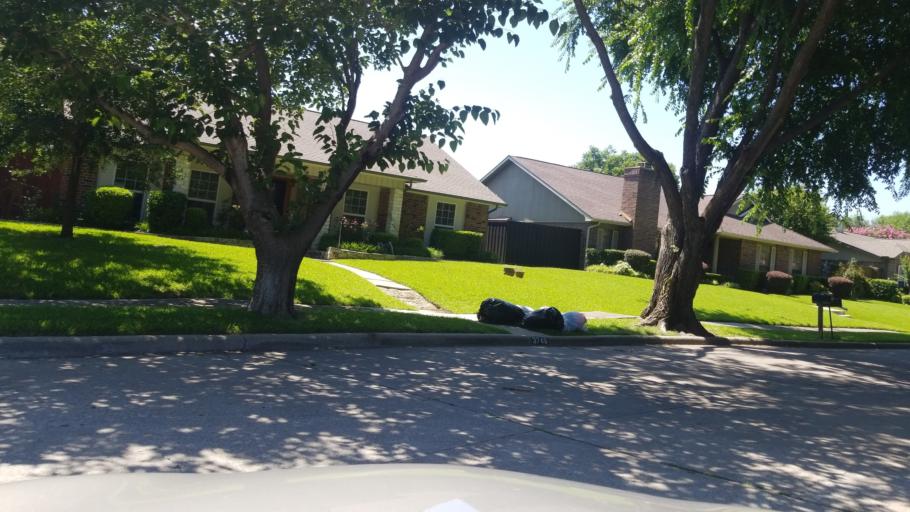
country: US
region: Texas
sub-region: Dallas County
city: Grand Prairie
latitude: 32.6825
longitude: -97.0062
